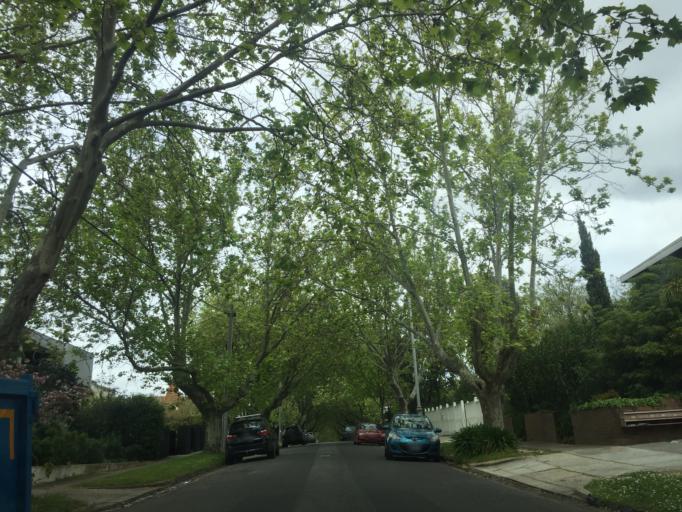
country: AU
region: Victoria
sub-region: Boroondara
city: Kew East
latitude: -37.8057
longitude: 145.0443
